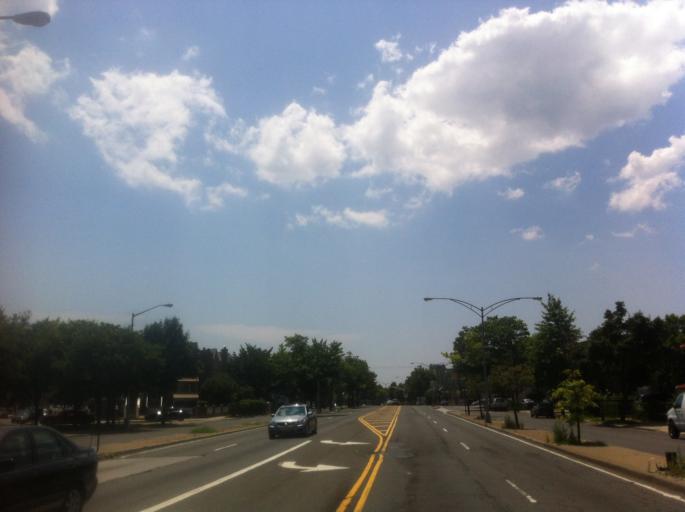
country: US
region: New York
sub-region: Kings County
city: Brooklyn
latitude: 40.6505
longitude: -73.9236
